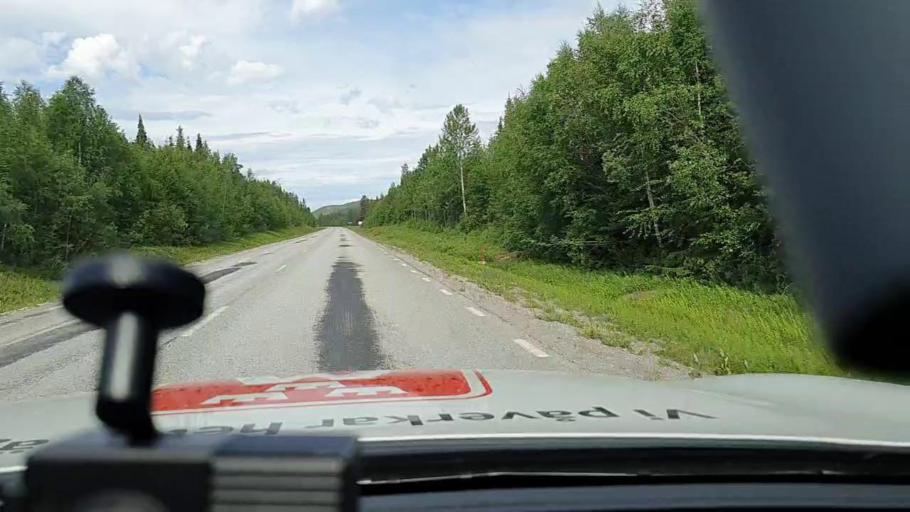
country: SE
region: Norrbotten
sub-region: Jokkmokks Kommun
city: Jokkmokk
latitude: 66.5502
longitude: 20.1224
